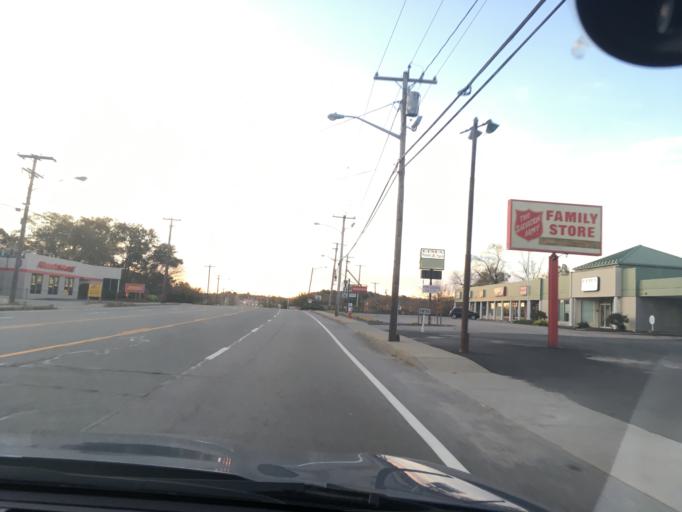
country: US
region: Rhode Island
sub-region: Kent County
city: East Greenwich
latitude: 41.6118
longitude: -71.4574
